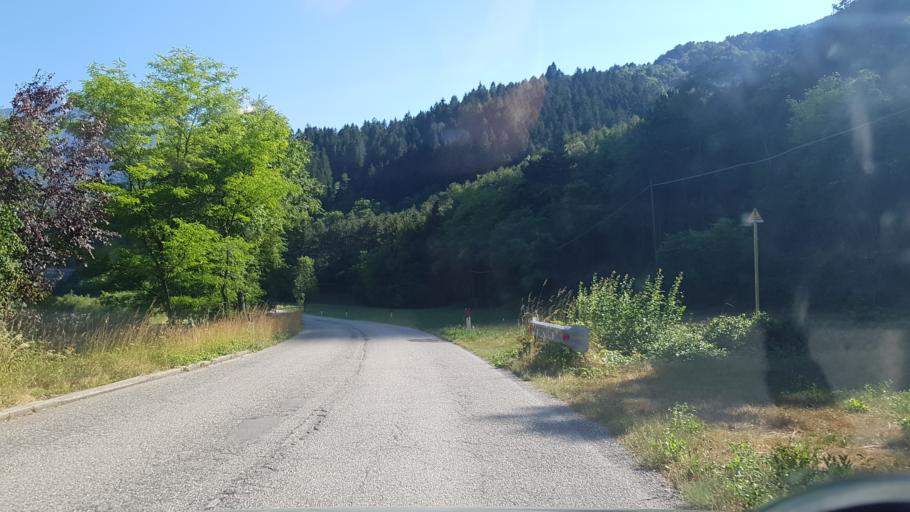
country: IT
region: Friuli Venezia Giulia
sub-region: Provincia di Udine
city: Moggio Udinese
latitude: 46.4204
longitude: 13.1983
